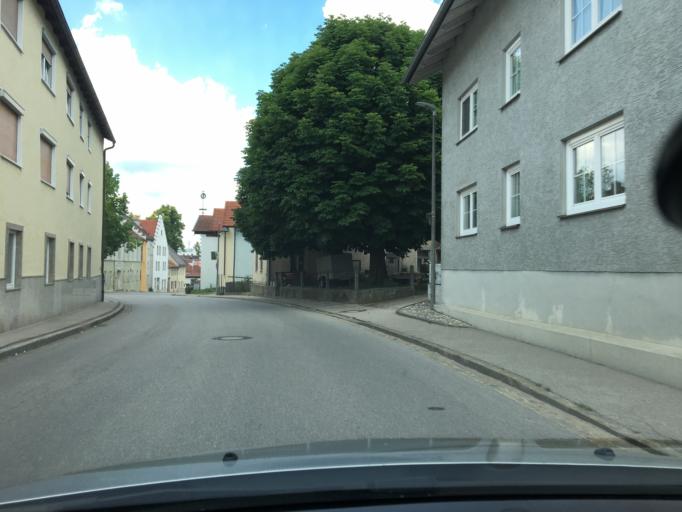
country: DE
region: Bavaria
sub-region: Upper Bavaria
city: Neumarkt-Sankt Veit
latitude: 48.3583
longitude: 12.5119
